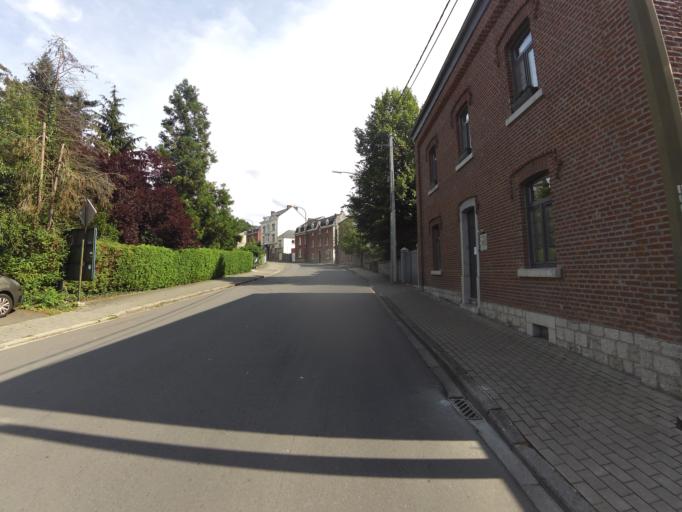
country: BE
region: Wallonia
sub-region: Province du Luxembourg
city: Durbuy
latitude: 50.3493
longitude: 5.4980
